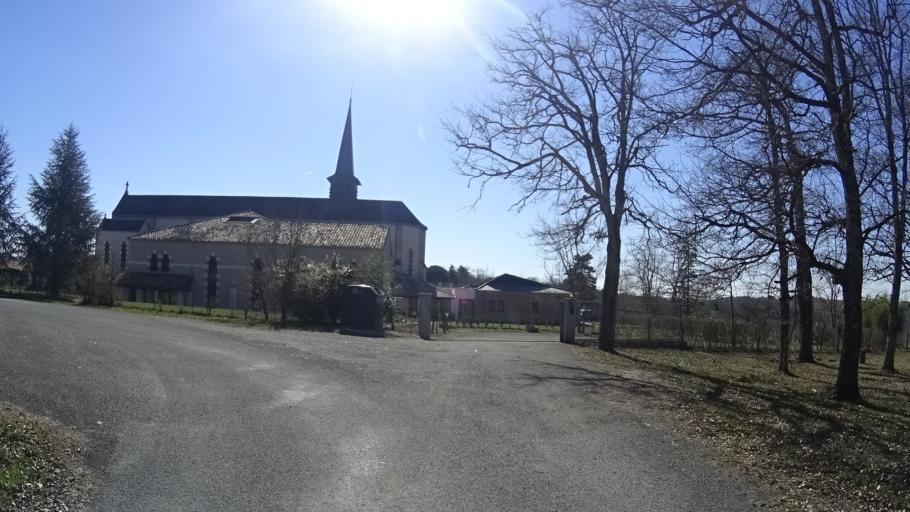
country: FR
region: Aquitaine
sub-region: Departement de la Dordogne
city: Saint-Aulaye
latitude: 45.1291
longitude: 0.2135
